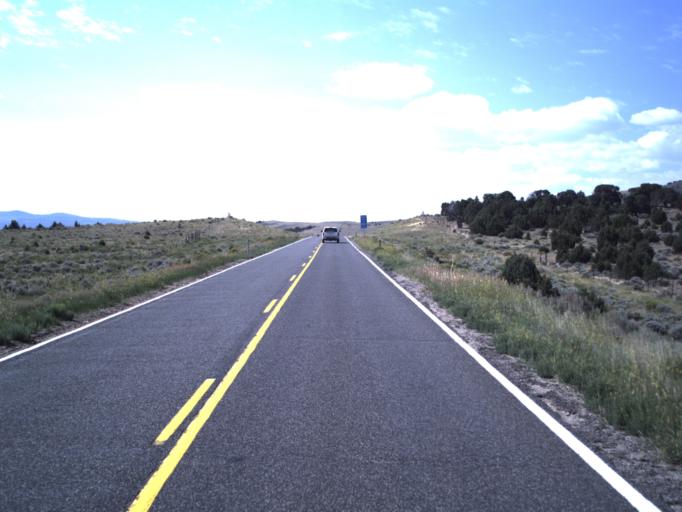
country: US
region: Utah
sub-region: Daggett County
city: Manila
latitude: 40.9950
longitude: -109.8432
